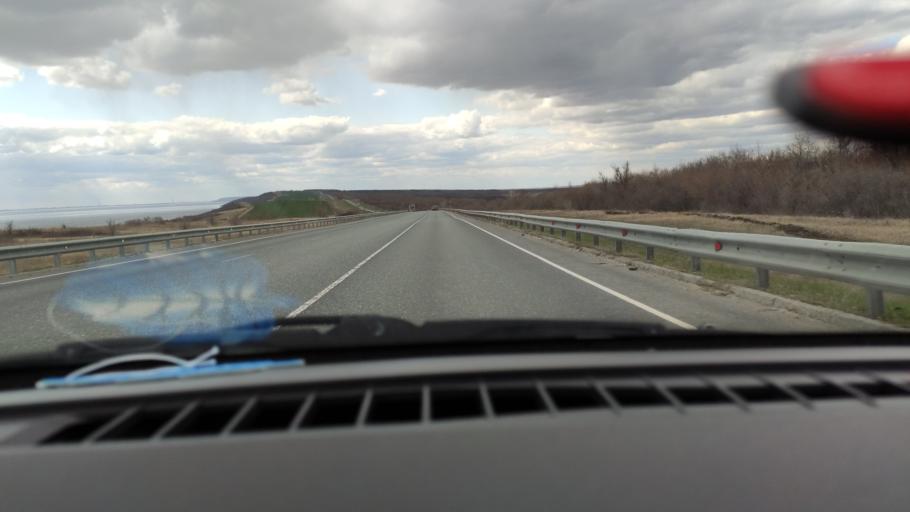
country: RU
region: Saratov
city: Balakovo
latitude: 52.1997
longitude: 47.8636
